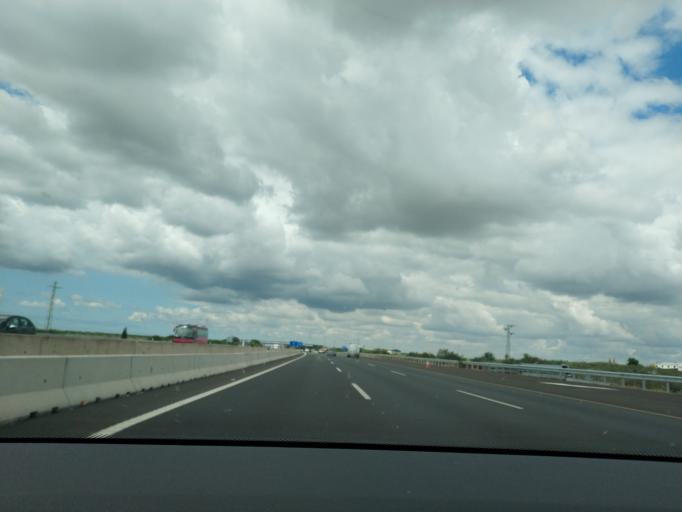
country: ES
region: Andalusia
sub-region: Provincia de Sevilla
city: Espartinas
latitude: 37.3637
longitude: -6.1265
